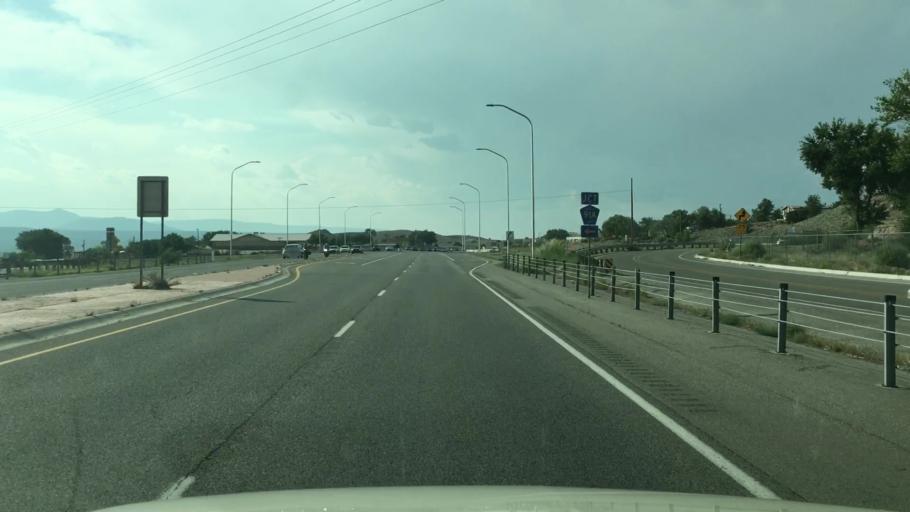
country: US
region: New Mexico
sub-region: Santa Fe County
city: El Valle de Arroyo Seco
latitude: 35.9680
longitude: -106.0362
